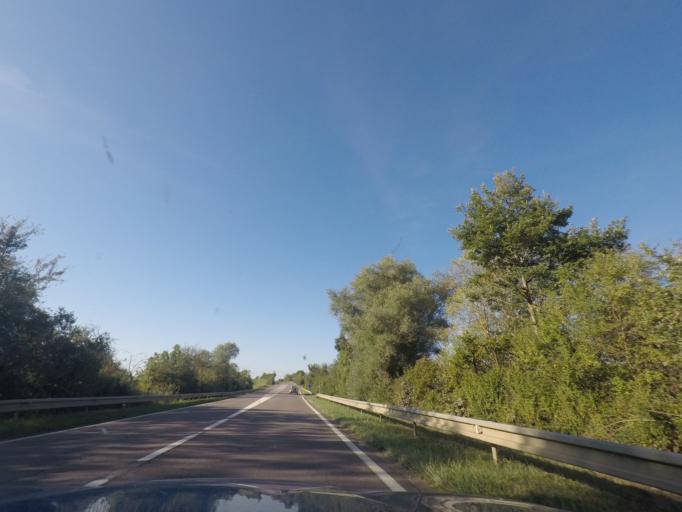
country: FR
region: Lorraine
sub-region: Departement de la Moselle
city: Hettange-Grande
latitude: 49.4414
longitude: 6.1697
